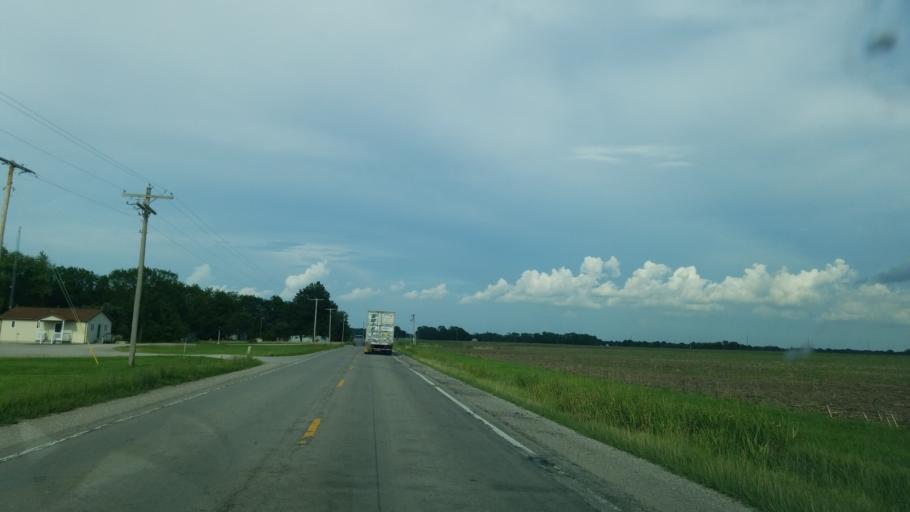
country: US
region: Illinois
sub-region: Marion County
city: Sandoval
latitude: 38.6166
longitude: -89.1517
